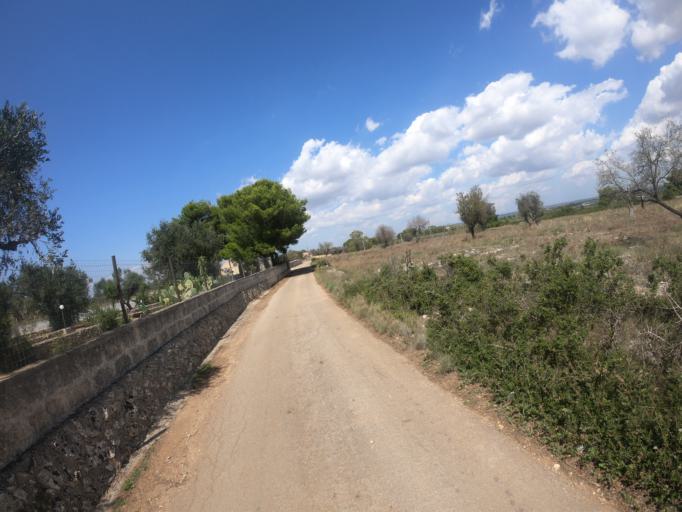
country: IT
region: Apulia
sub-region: Provincia di Lecce
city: Galatone
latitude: 40.1229
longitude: 18.0788
